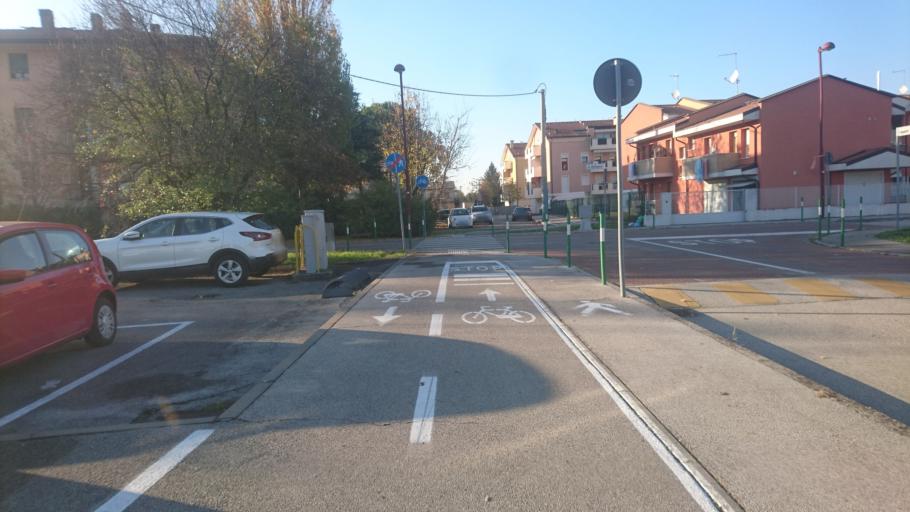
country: IT
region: Veneto
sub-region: Provincia di Padova
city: Villaguattera
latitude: 45.4451
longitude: 11.8186
